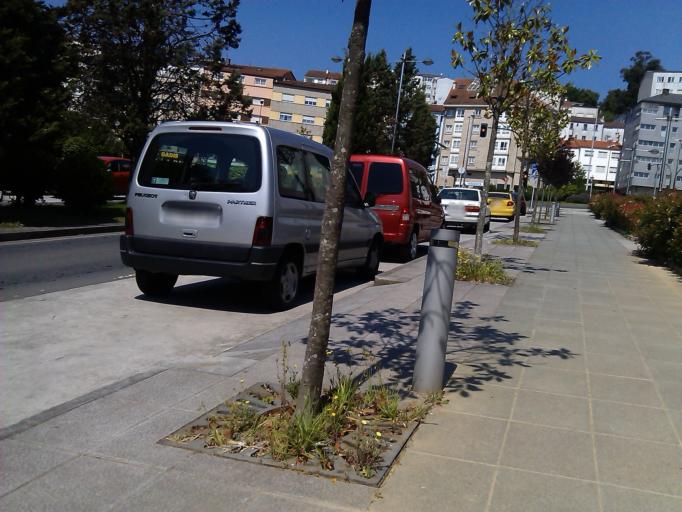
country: ES
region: Galicia
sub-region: Provincia da Coruna
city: Santiago de Compostela
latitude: 42.8842
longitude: -8.5323
